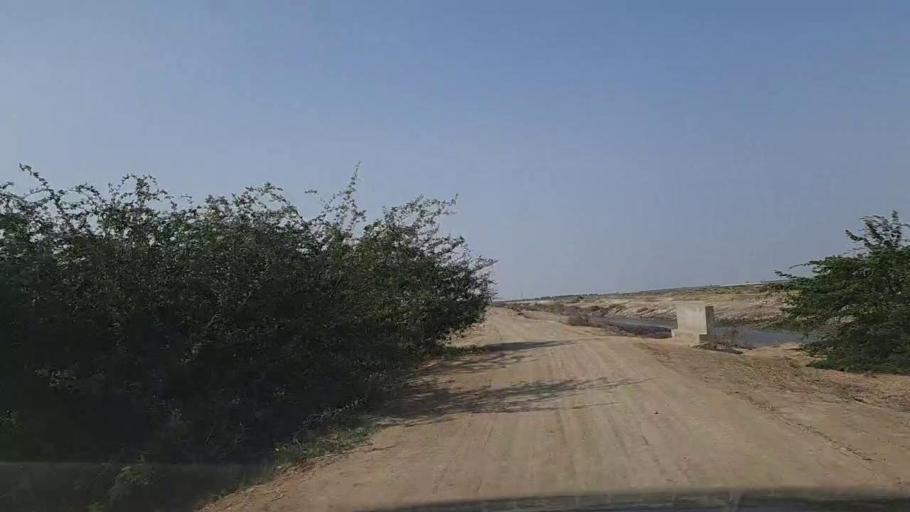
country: PK
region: Sindh
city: Gharo
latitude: 24.7047
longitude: 67.5738
